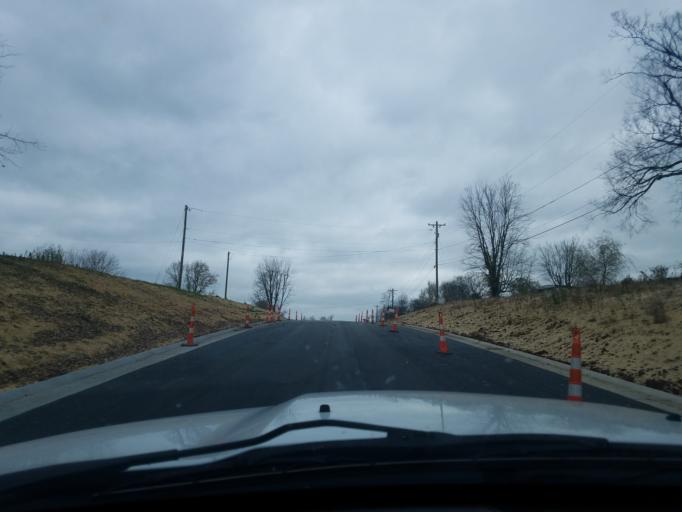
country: US
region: Kentucky
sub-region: Jefferson County
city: Prospect
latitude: 38.3375
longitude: -85.6560
